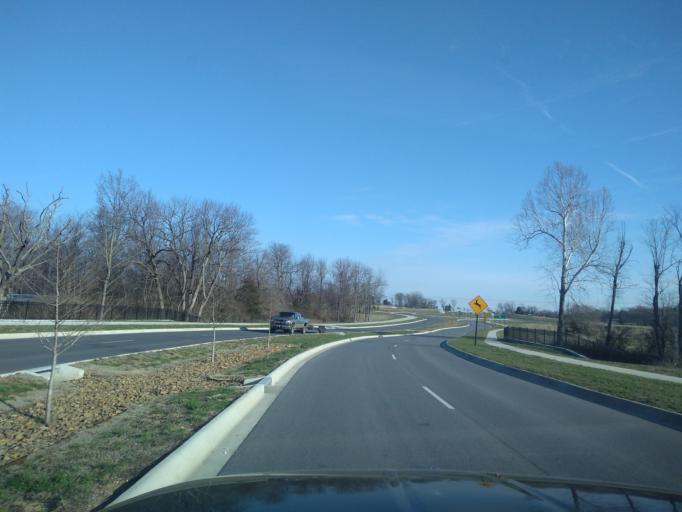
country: US
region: Arkansas
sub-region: Washington County
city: Farmington
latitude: 36.0489
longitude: -94.2199
